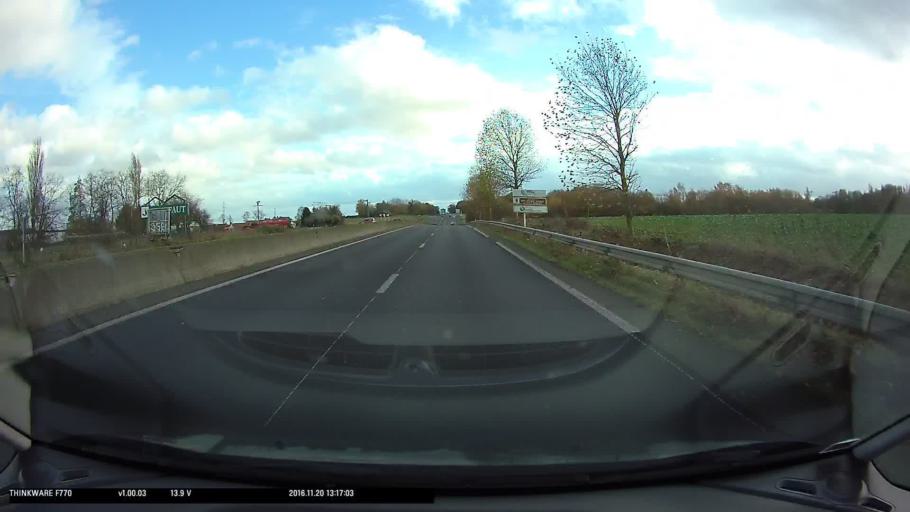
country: FR
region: Ile-de-France
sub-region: Departement du Val-d'Oise
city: Courdimanche
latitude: 49.0600
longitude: 1.9974
